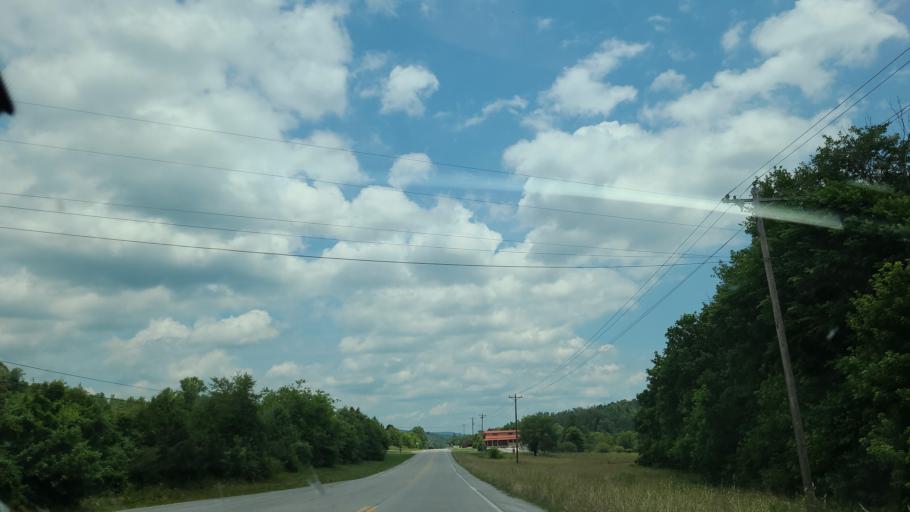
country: US
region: Tennessee
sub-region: Bledsoe County
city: Pikeville
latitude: 35.6334
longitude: -85.1745
